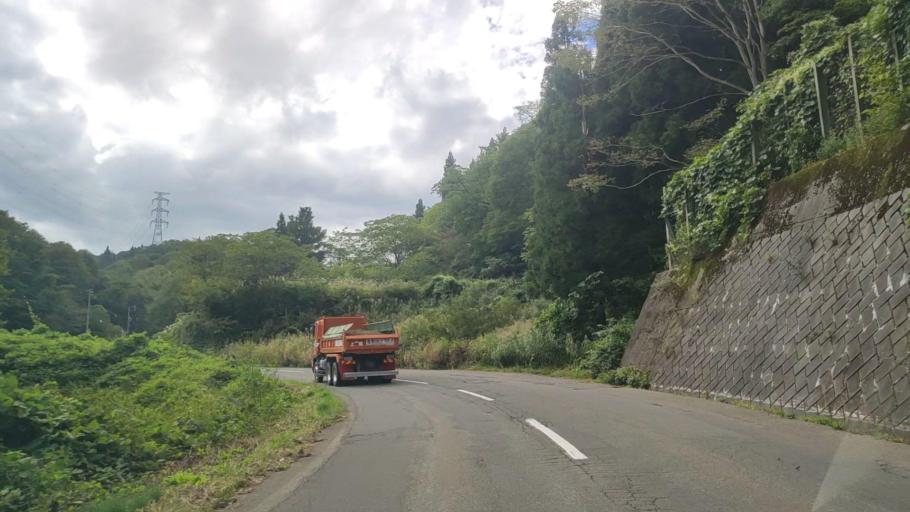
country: JP
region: Nagano
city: Iiyama
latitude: 36.8887
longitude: 138.3229
